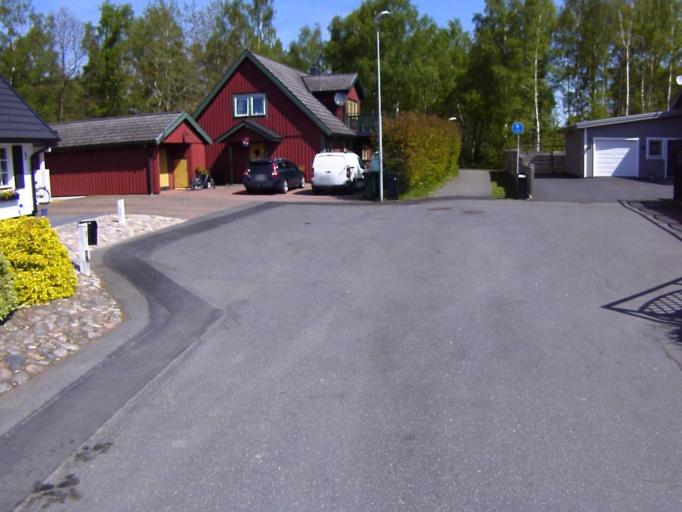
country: SE
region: Skane
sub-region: Kristianstads Kommun
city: Onnestad
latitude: 55.9396
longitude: 13.9817
